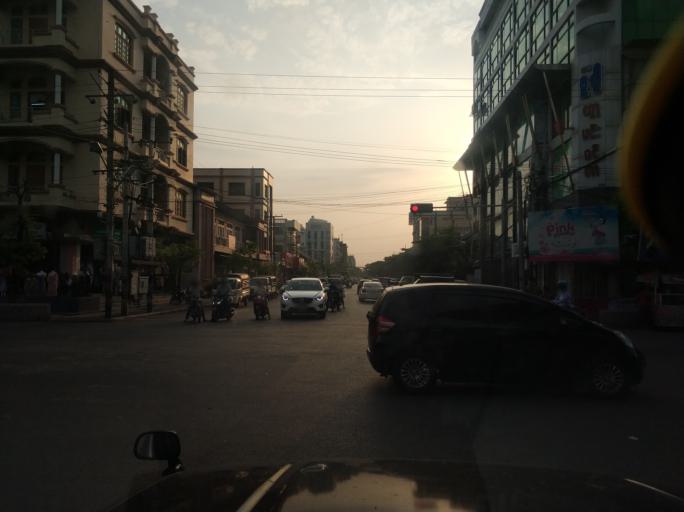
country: MM
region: Mandalay
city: Mandalay
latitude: 21.9771
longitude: 96.0842
